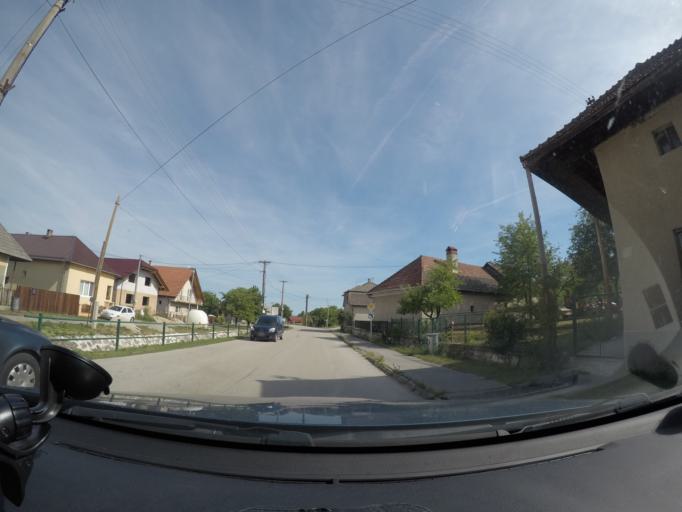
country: SK
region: Trenciansky
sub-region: Okres Trencin
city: Trencin
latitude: 48.7608
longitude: 18.1097
